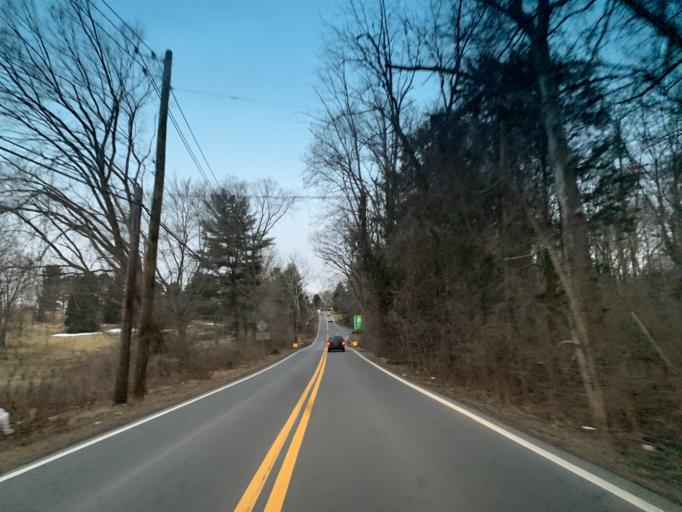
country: US
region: Maryland
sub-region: Montgomery County
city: Layhill
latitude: 39.1164
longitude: -77.0367
